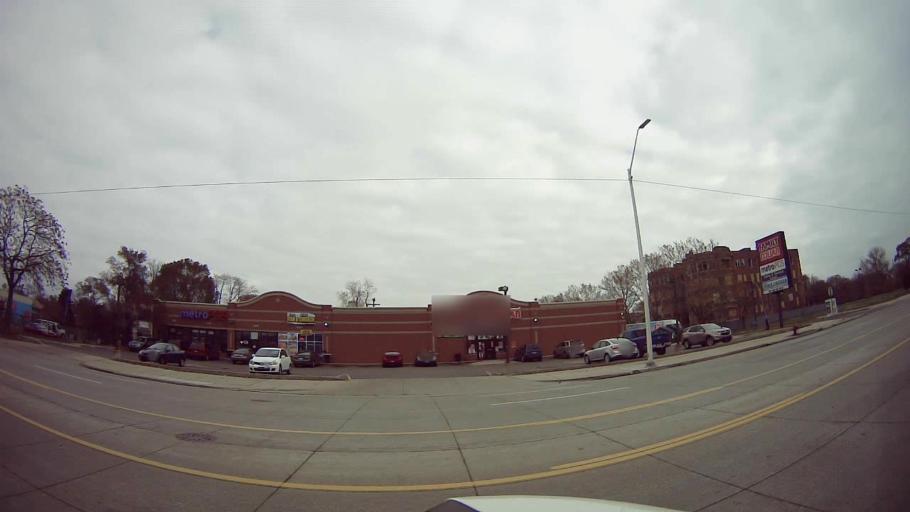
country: US
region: Michigan
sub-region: Wayne County
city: Hamtramck
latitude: 42.3783
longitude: -83.0787
